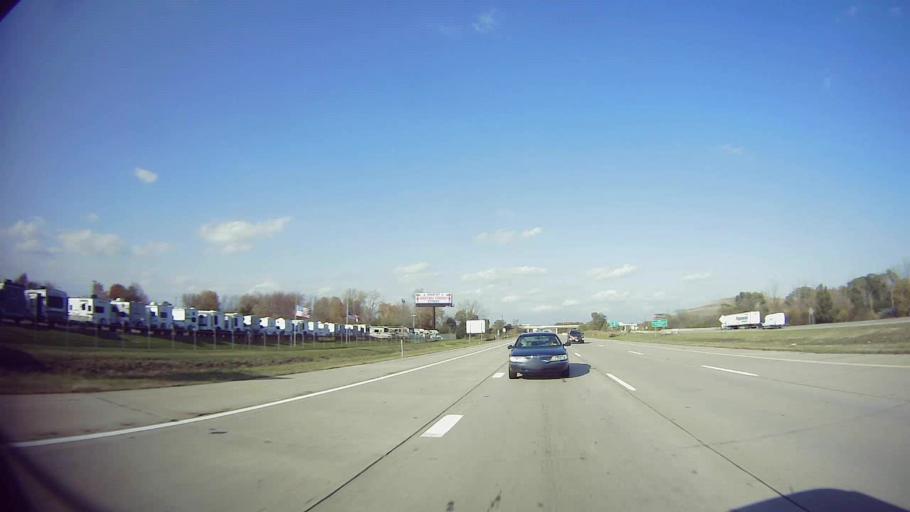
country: US
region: Michigan
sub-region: Wayne County
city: Woodhaven
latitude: 42.1800
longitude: -83.2436
